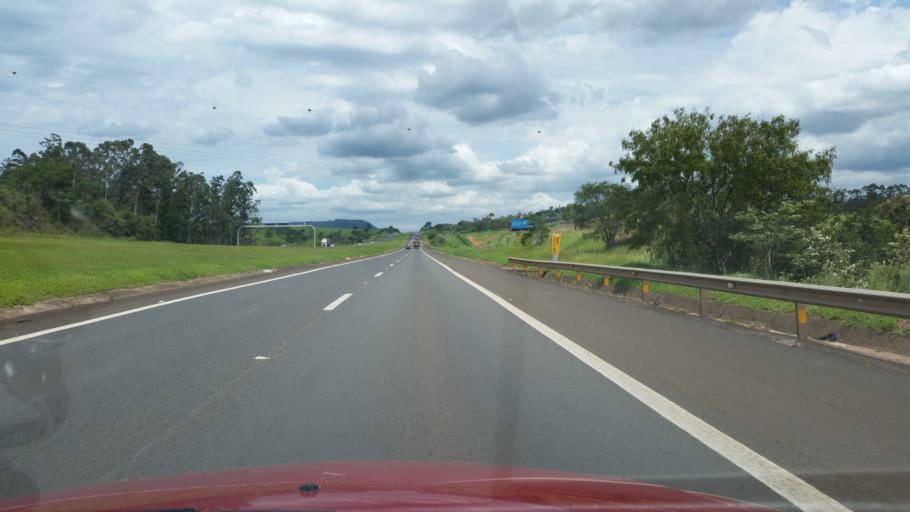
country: BR
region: Sao Paulo
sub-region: Itatinga
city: Itatinga
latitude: -23.1400
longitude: -48.4337
